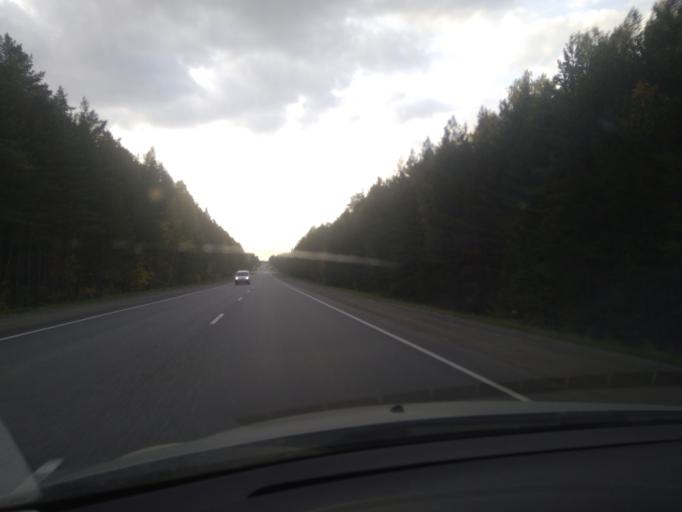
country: RU
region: Sverdlovsk
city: Verkhneye Dubrovo
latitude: 56.6950
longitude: 61.0968
